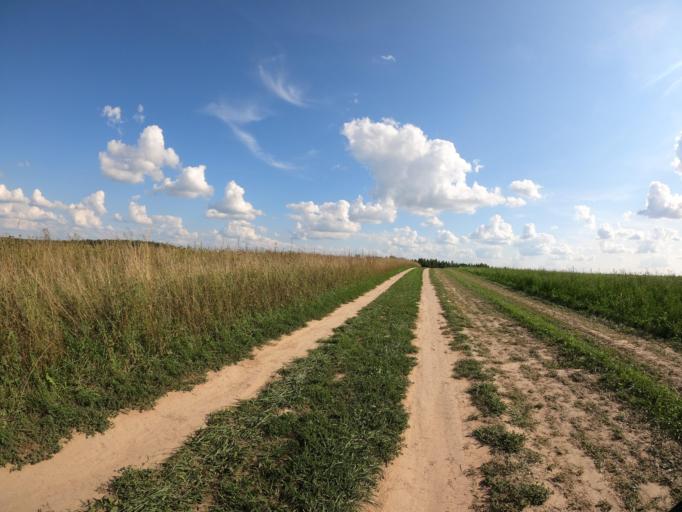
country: RU
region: Moskovskaya
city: Troitskoye
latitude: 55.2210
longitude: 38.4865
